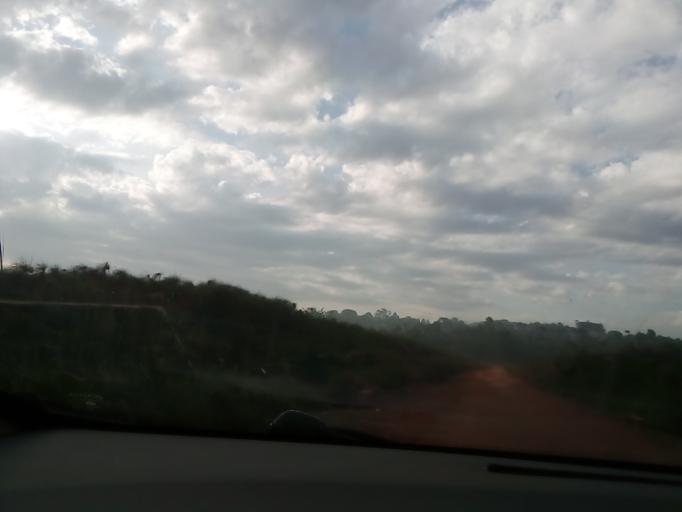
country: UG
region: Central Region
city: Masaka
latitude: -0.3456
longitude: 31.7082
